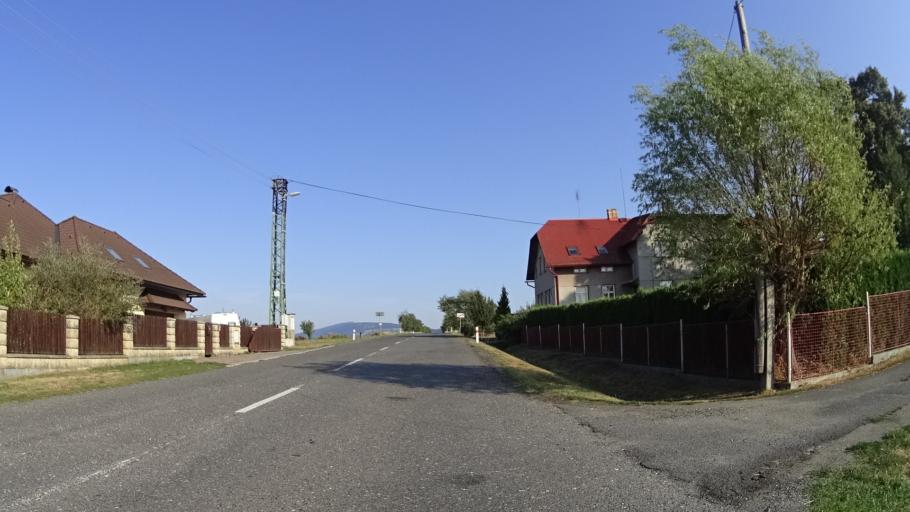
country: CZ
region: Liberecky
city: Hodkovice nad Mohelkou
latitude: 50.6420
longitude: 15.1096
